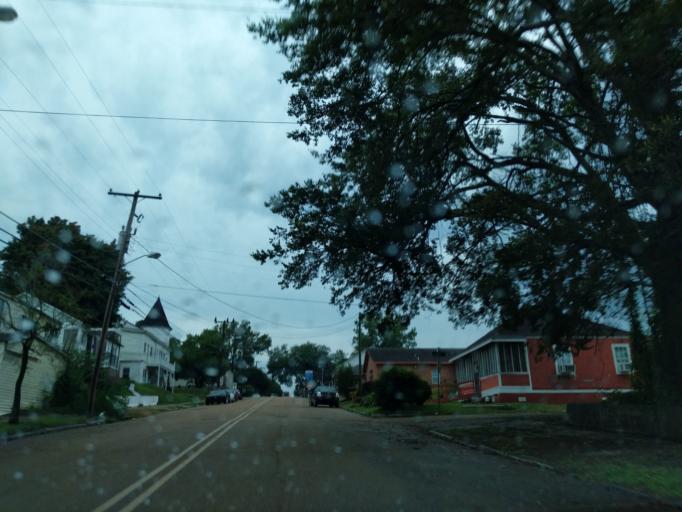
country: US
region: Mississippi
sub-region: Warren County
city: Vicksburg
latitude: 32.3557
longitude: -90.8776
